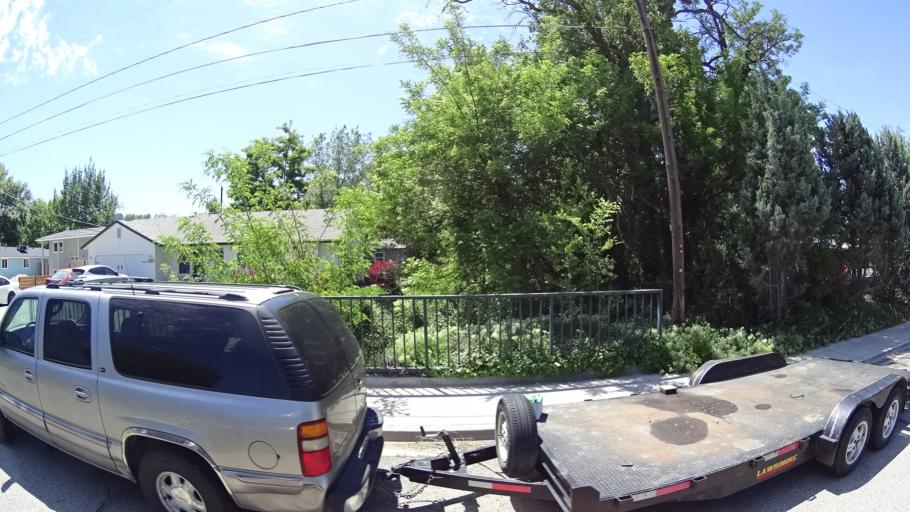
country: US
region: Idaho
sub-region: Ada County
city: Garden City
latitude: 43.6044
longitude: -116.2264
